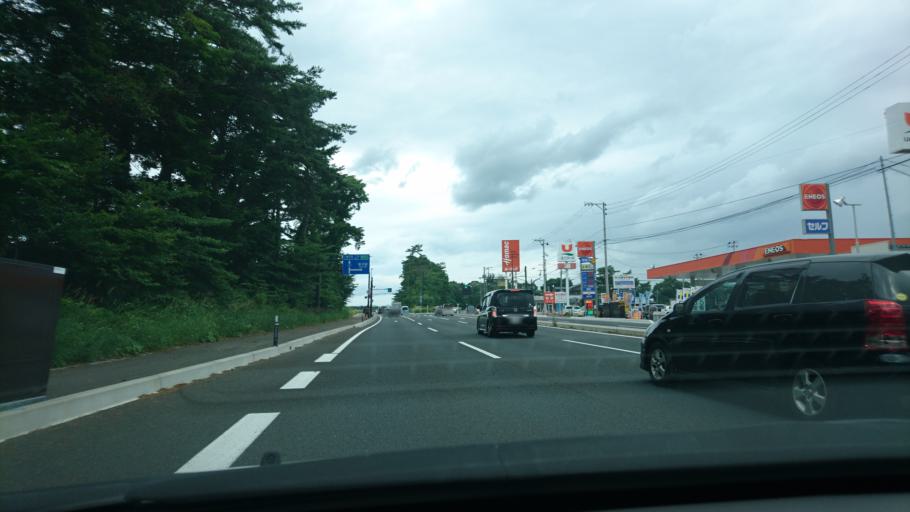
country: JP
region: Iwate
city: Morioka-shi
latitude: 39.7733
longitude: 141.1282
